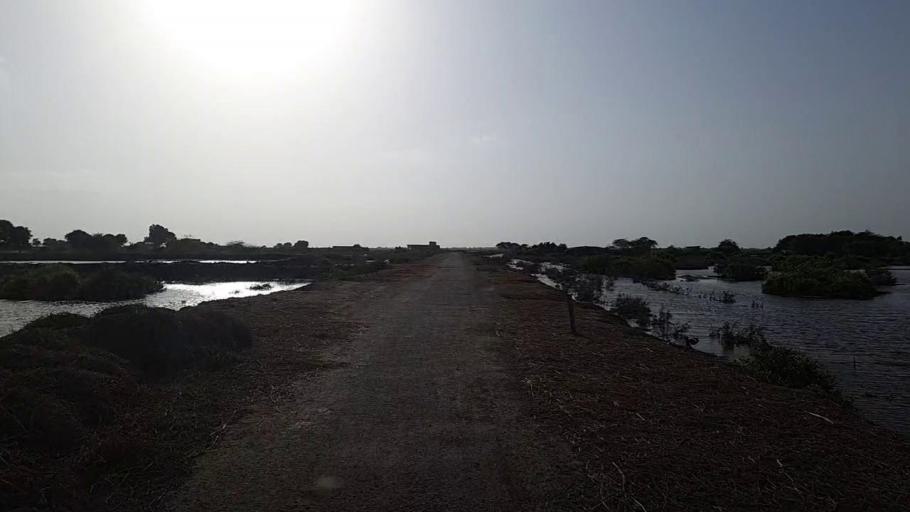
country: PK
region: Sindh
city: Kario
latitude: 24.6705
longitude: 68.4607
